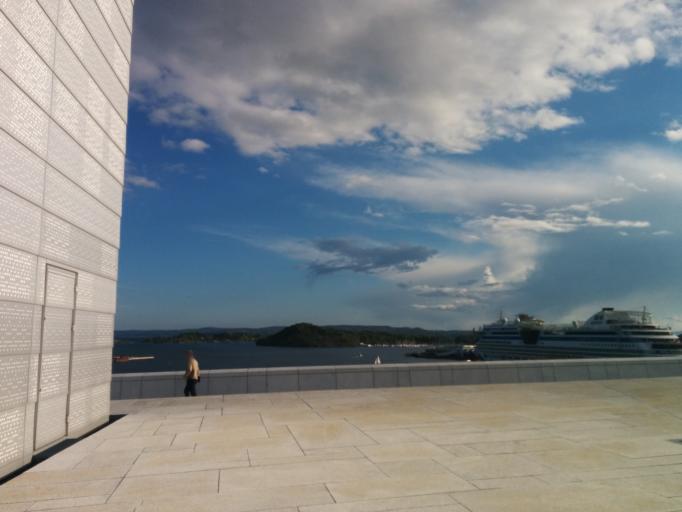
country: NO
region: Oslo
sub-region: Oslo
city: Oslo
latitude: 59.9073
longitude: 10.7526
